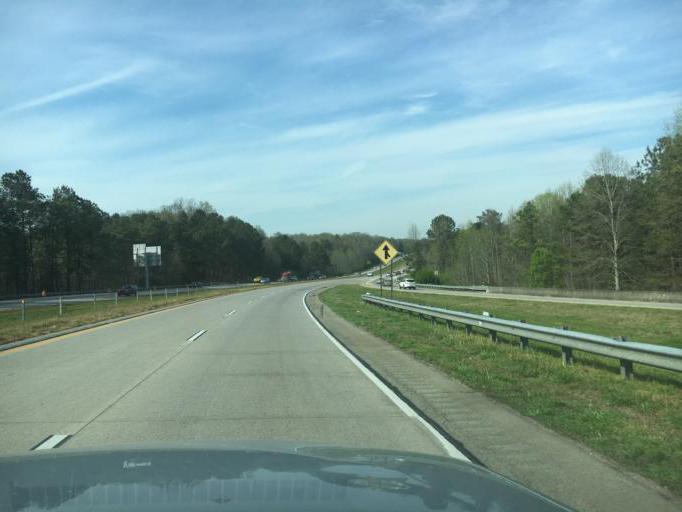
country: US
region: Georgia
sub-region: Hall County
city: Gainesville
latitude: 34.3188
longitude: -83.7888
